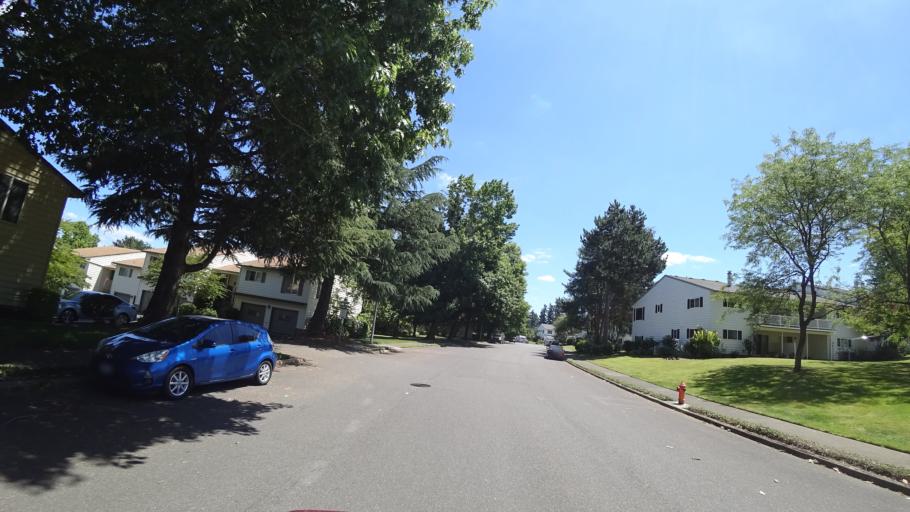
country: US
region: Oregon
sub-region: Multnomah County
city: Fairview
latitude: 45.5450
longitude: -122.5081
